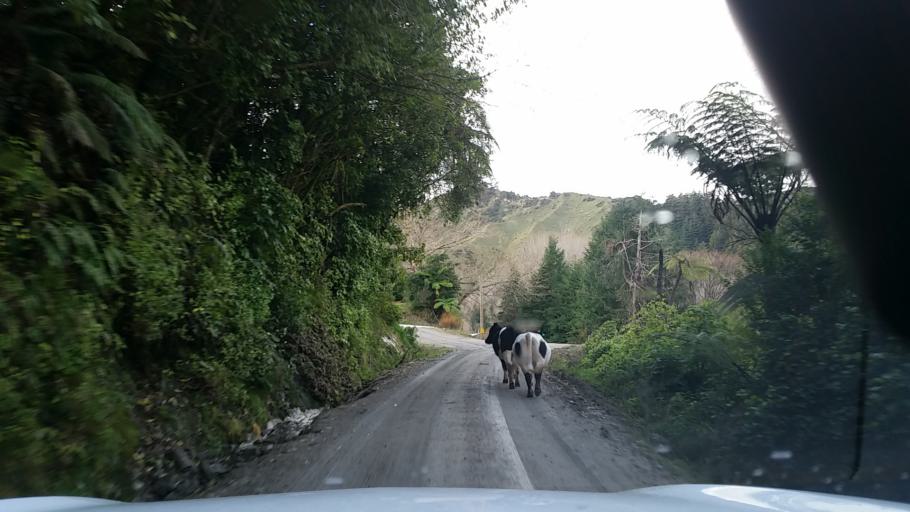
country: NZ
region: Taranaki
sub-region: South Taranaki District
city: Patea
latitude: -39.5619
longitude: 174.8042
